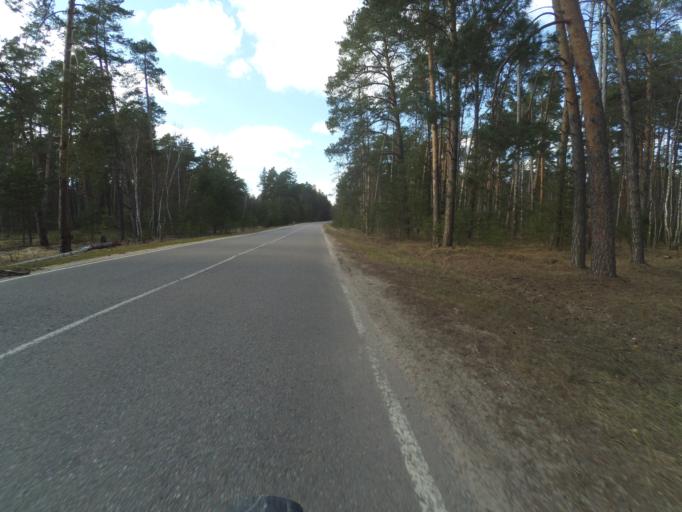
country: RU
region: Moskovskaya
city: Stupino
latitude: 54.8591
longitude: 37.8609
